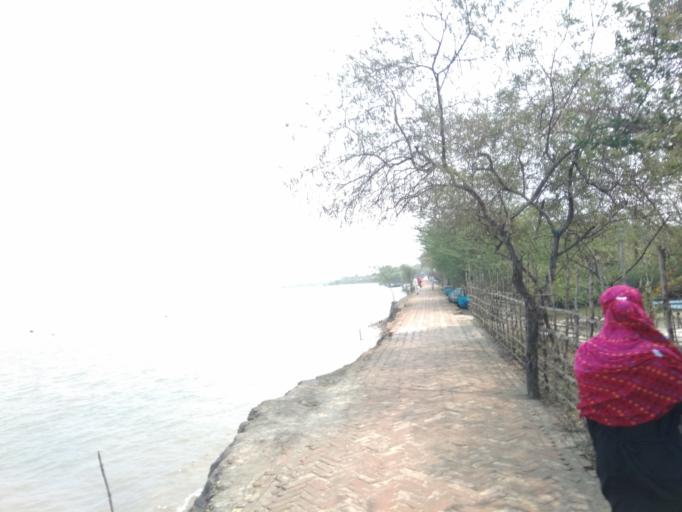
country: IN
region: West Bengal
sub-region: North 24 Parganas
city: Taki
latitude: 22.2811
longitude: 89.2864
